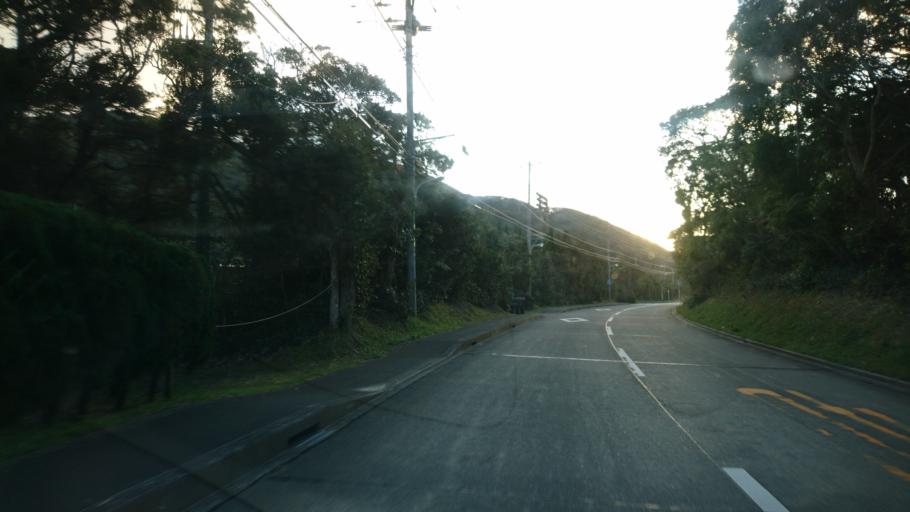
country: JP
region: Shizuoka
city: Shimoda
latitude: 34.3639
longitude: 139.2572
